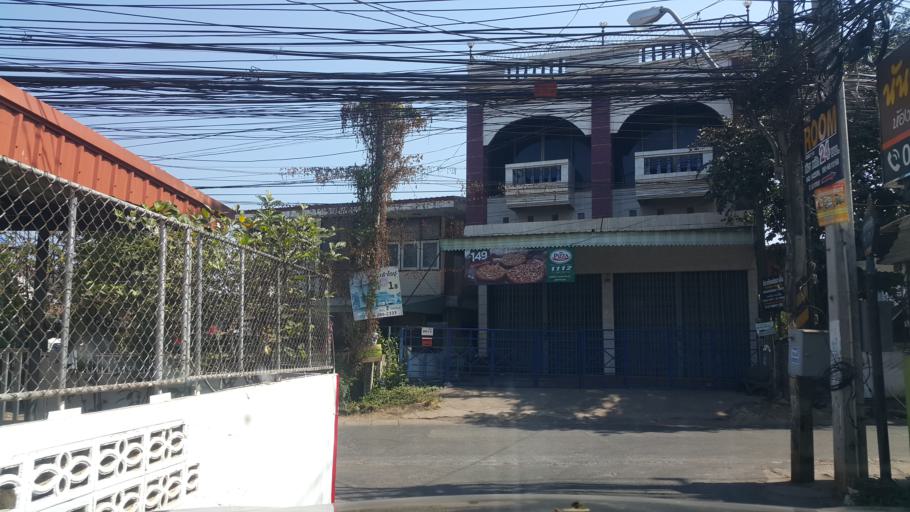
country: TH
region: Changwat Udon Thani
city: Udon Thani
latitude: 17.3924
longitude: 102.8095
